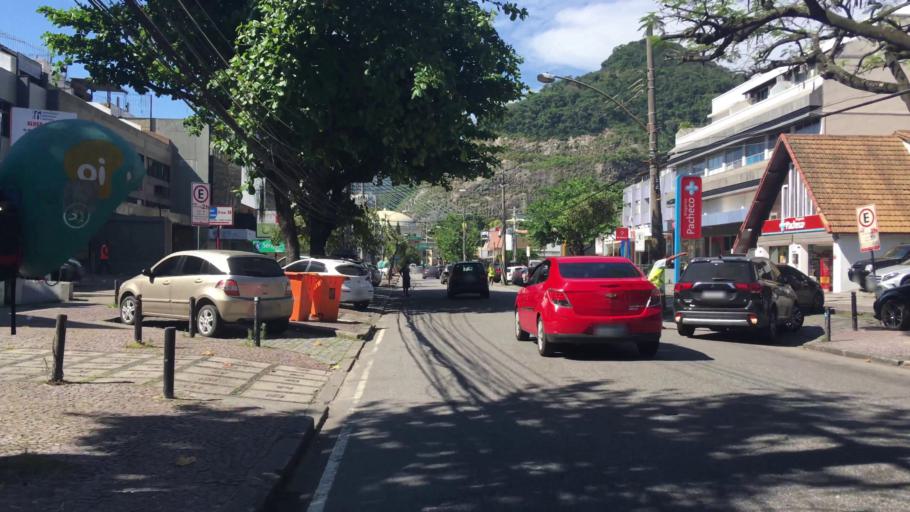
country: BR
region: Rio de Janeiro
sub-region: Rio De Janeiro
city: Rio de Janeiro
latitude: -23.0103
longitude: -43.3048
